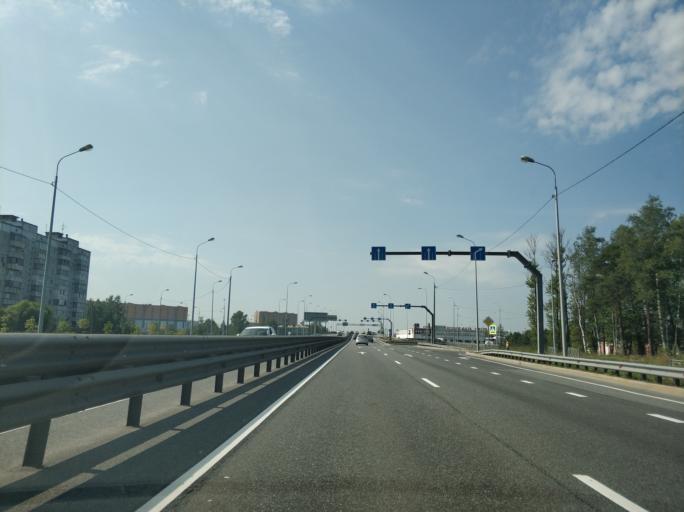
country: RU
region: St.-Petersburg
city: Krasnogvargeisky
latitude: 59.9861
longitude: 30.5195
